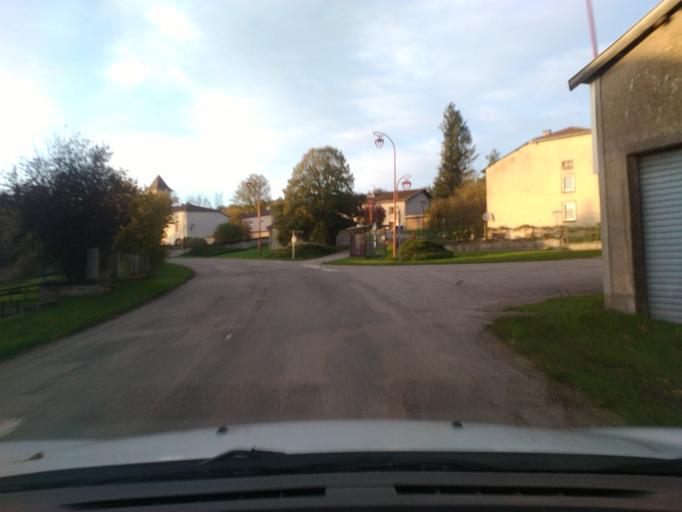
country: FR
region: Lorraine
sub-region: Departement des Vosges
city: Mirecourt
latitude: 48.2567
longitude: 6.1938
